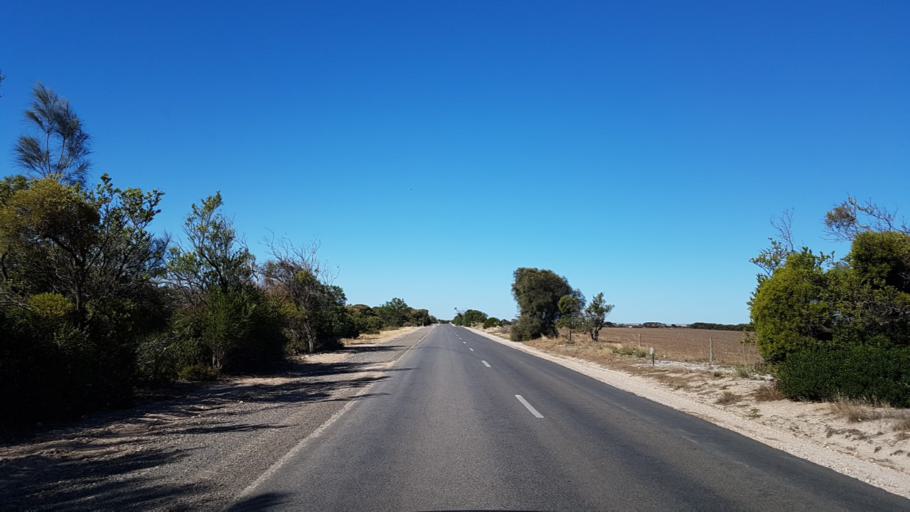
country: AU
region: South Australia
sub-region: Yorke Peninsula
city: Honiton
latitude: -34.9307
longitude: 137.4480
